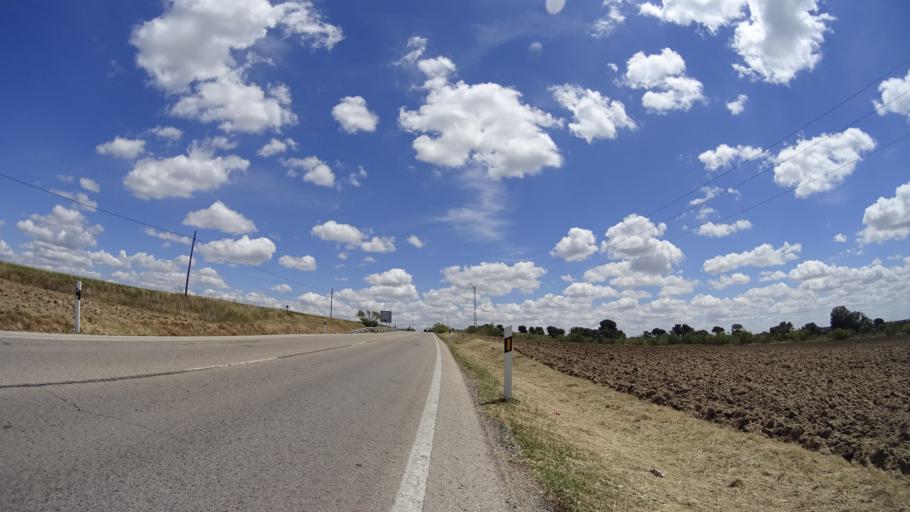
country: ES
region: Madrid
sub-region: Provincia de Madrid
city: Boadilla del Monte
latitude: 40.4129
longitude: -3.9325
